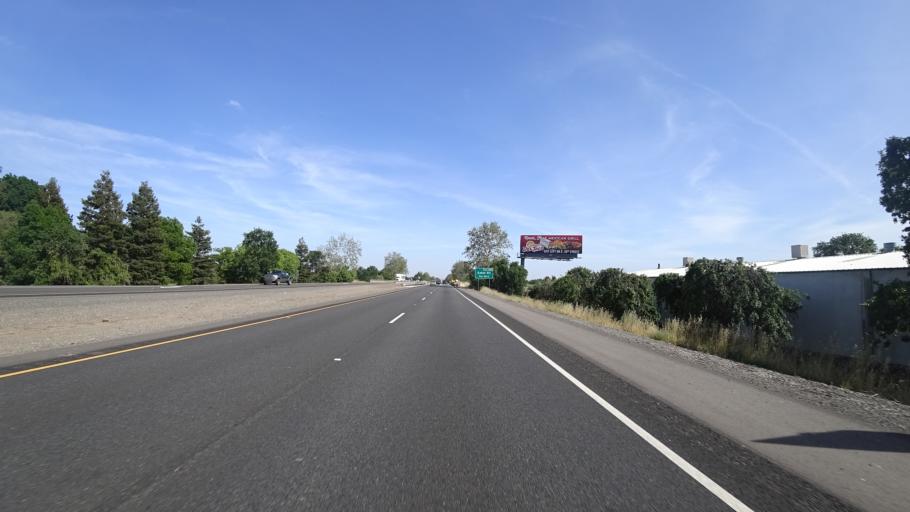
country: US
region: California
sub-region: Butte County
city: Chico
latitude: 39.7854
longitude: -121.8871
